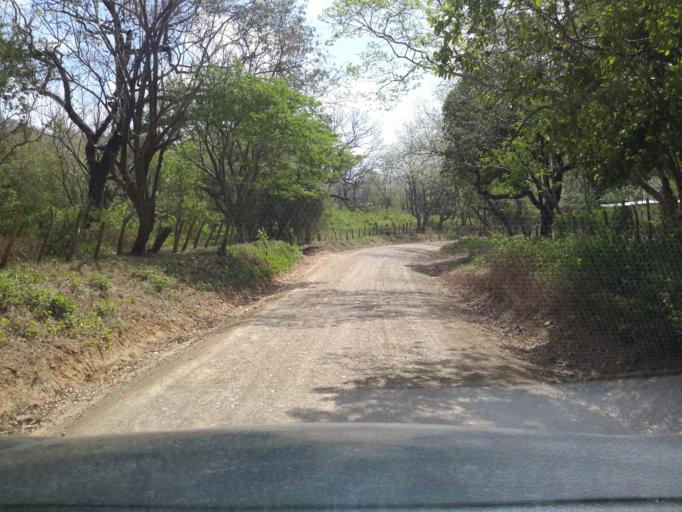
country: NI
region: Rivas
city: San Juan del Sur
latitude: 11.2183
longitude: -85.8124
